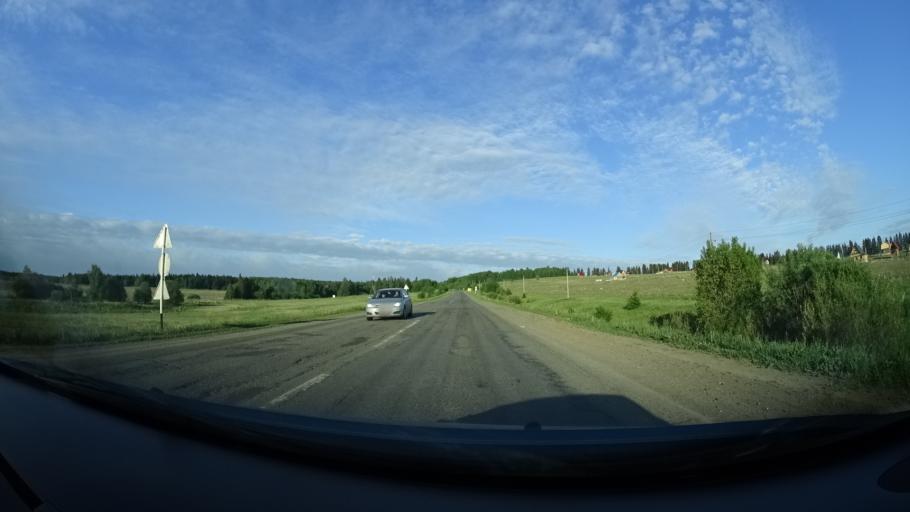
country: RU
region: Perm
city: Kultayevo
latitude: 57.8502
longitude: 55.8432
